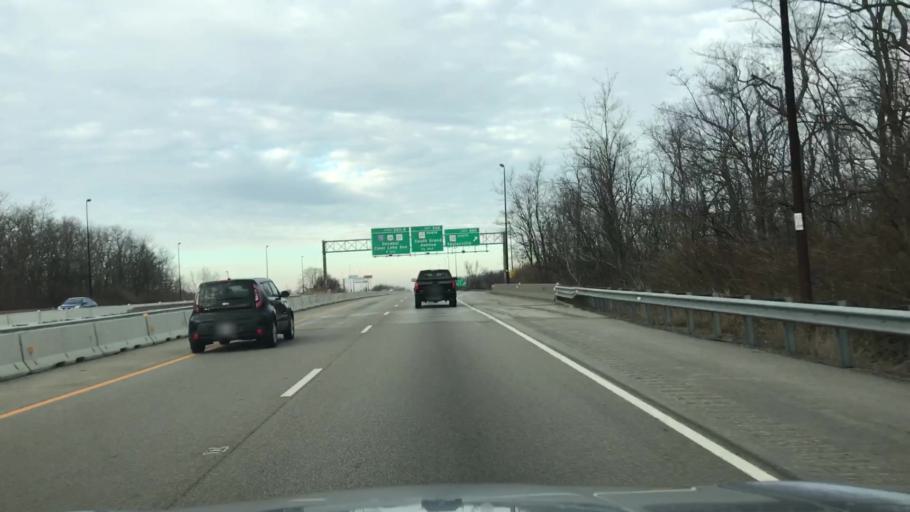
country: US
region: Illinois
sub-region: Sangamon County
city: Grandview
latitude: 39.7822
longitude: -89.6003
